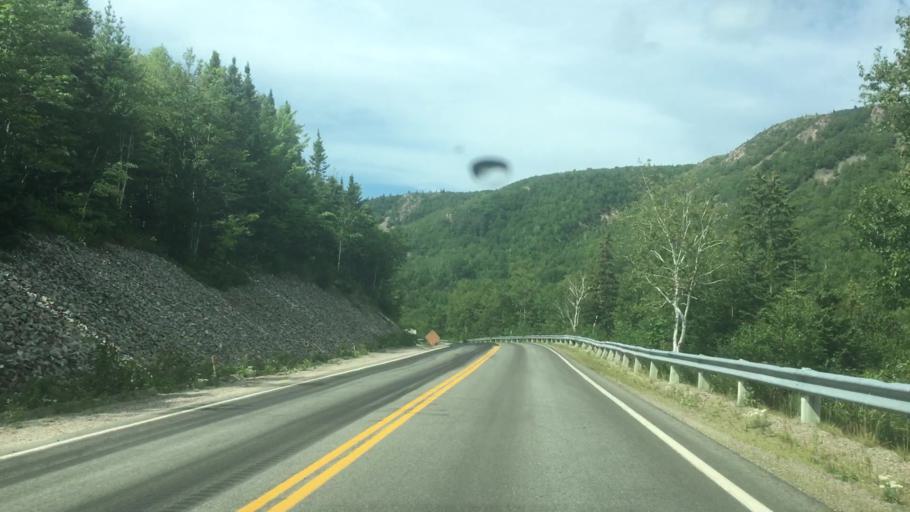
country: CA
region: Nova Scotia
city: Sydney Mines
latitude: 46.5793
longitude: -60.3898
